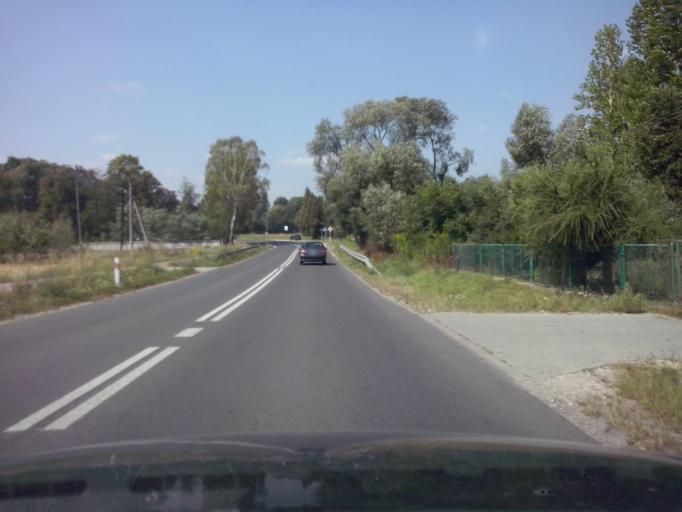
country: PL
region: Swietokrzyskie
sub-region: Powiat buski
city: Gnojno
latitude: 50.6055
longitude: 20.8371
